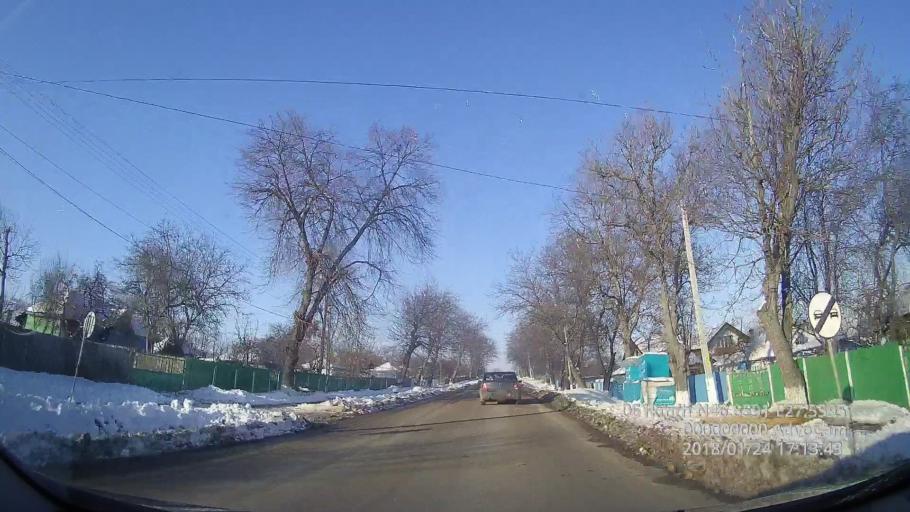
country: RO
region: Vaslui
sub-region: Comuna Rebricea
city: Rebricea
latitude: 46.8597
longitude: 27.5594
